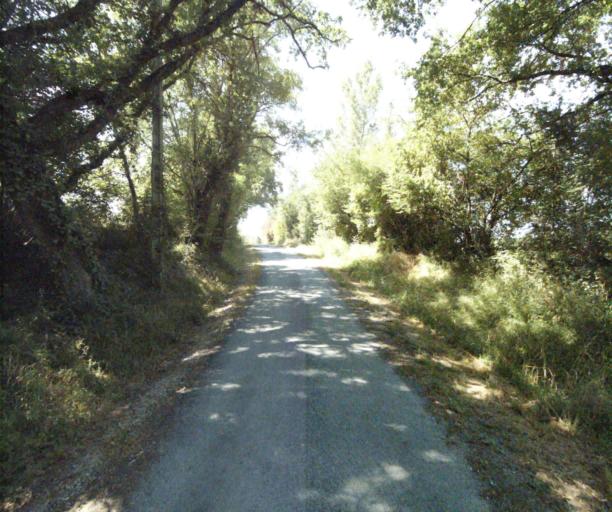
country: FR
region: Midi-Pyrenees
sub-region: Departement du Tarn
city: Puylaurens
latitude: 43.5339
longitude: 2.0058
